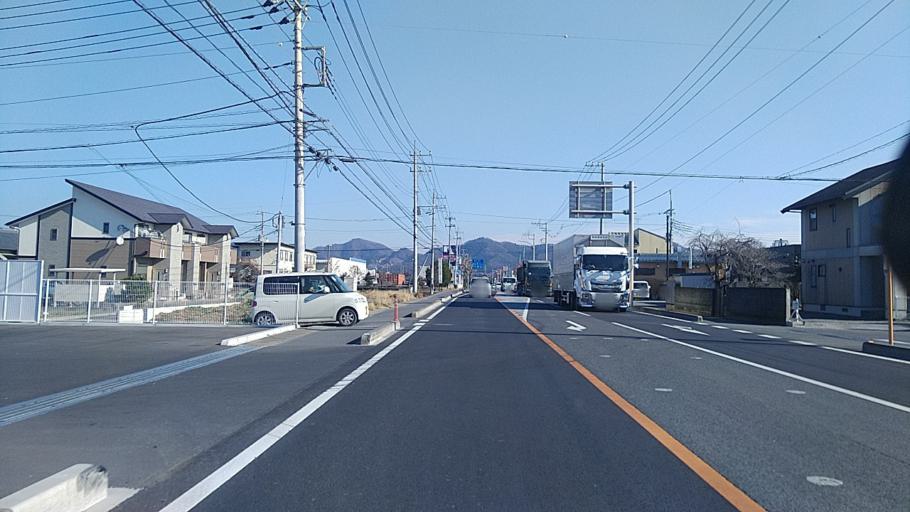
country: JP
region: Tochigi
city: Tanuma
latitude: 36.3677
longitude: 139.5687
